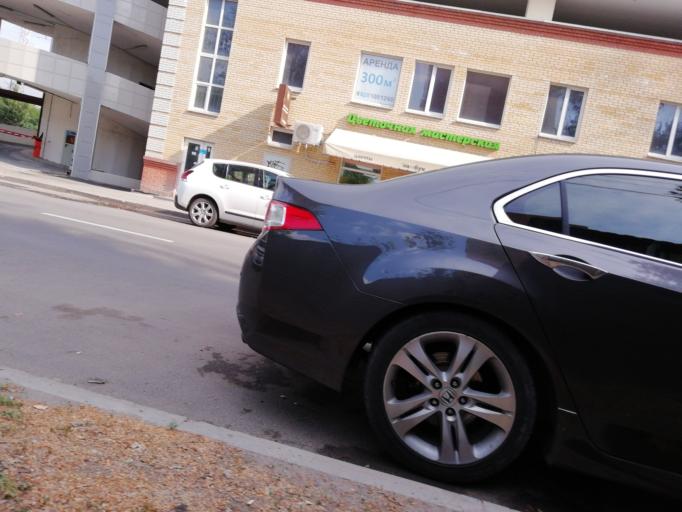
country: RU
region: Rostov
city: Severnyy
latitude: 47.2733
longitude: 39.7161
